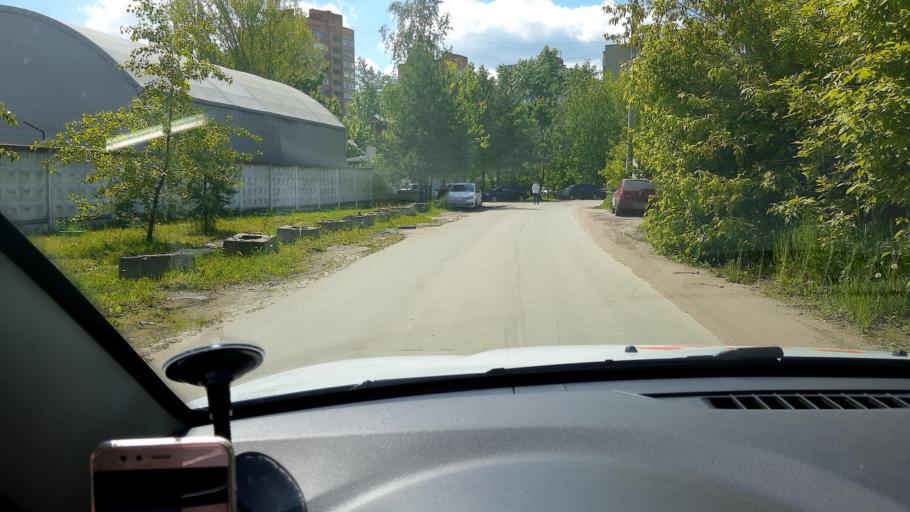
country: RU
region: Nizjnij Novgorod
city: Burevestnik
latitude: 56.2303
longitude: 43.8843
